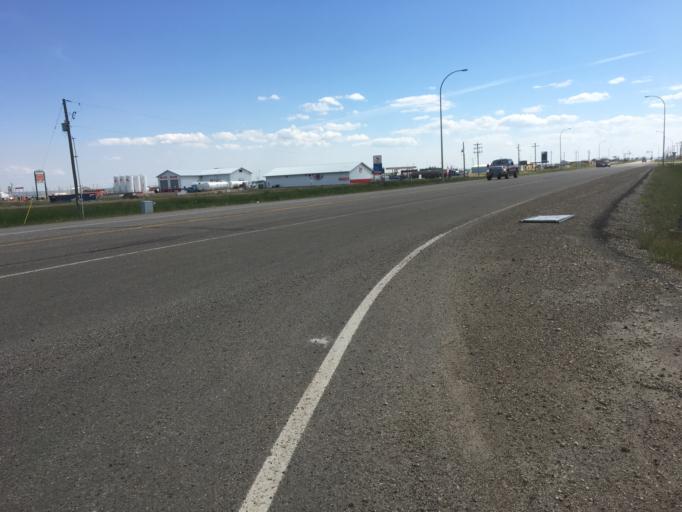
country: CA
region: Alberta
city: Spirit River
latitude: 55.7595
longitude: -118.6987
